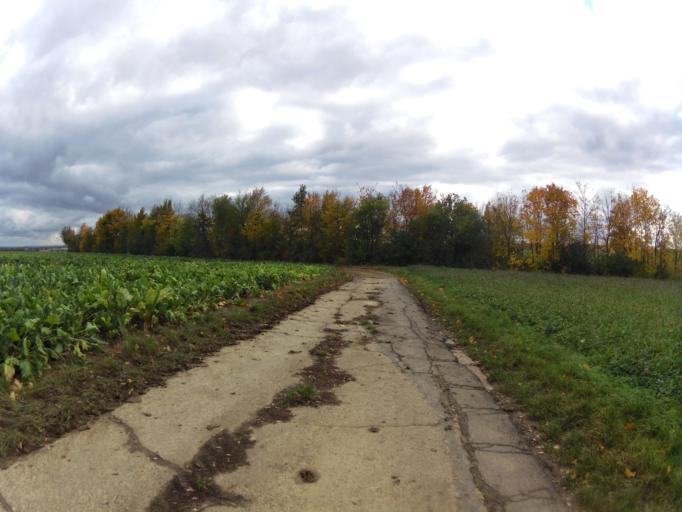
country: DE
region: Bavaria
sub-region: Regierungsbezirk Unterfranken
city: Kurnach
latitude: 49.8737
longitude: 10.0123
